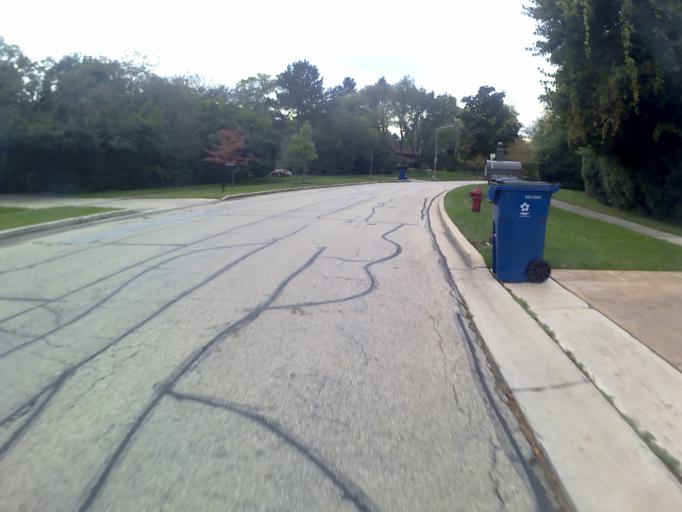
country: US
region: Illinois
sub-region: DuPage County
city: Lisle
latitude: 41.8135
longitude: -88.0959
